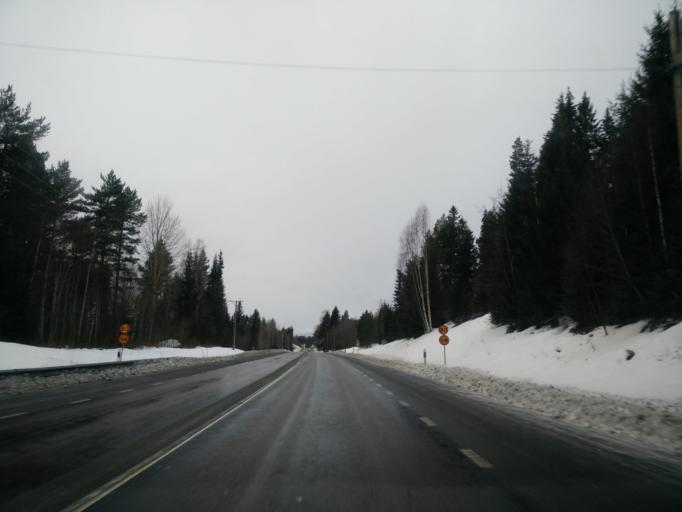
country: SE
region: Vaesternorrland
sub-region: Sundsvalls Kommun
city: Matfors
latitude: 62.4106
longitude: 16.6633
